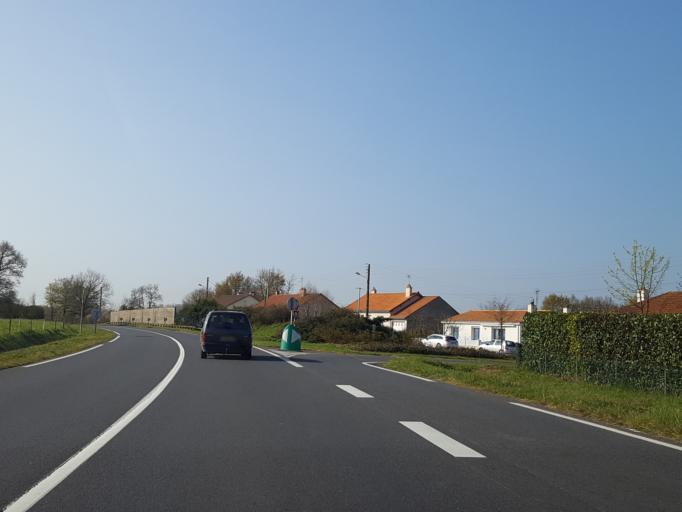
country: FR
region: Pays de la Loire
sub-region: Departement de la Vendee
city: Saint-Philbert-de-Bouaine
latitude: 46.9816
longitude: -1.5190
